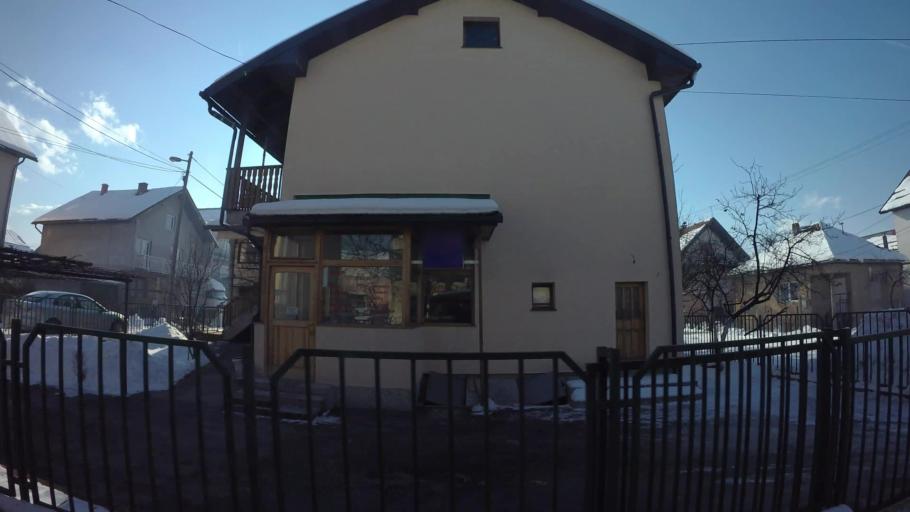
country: BA
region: Federation of Bosnia and Herzegovina
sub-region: Kanton Sarajevo
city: Sarajevo
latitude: 43.8170
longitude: 18.3254
